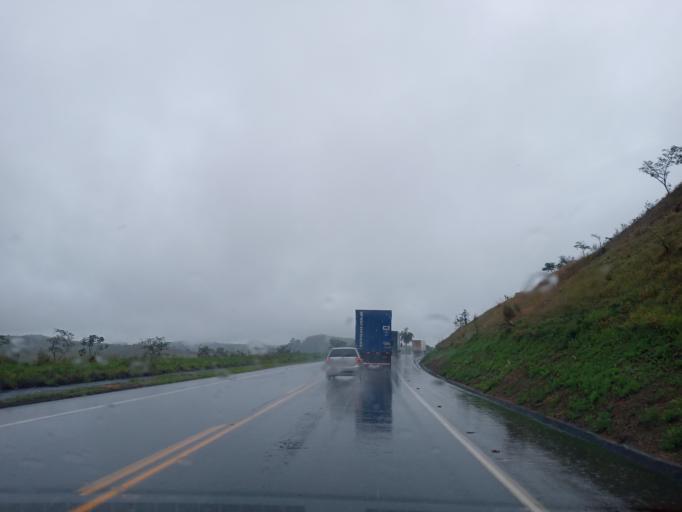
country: BR
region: Minas Gerais
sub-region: Luz
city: Luz
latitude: -19.7294
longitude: -45.8662
